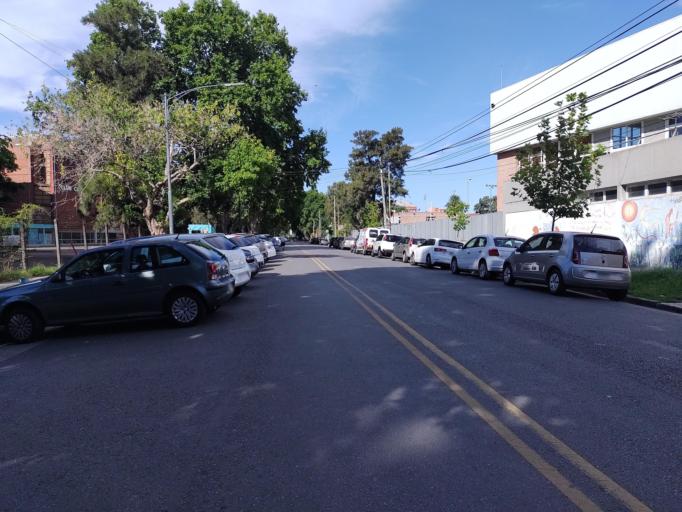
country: AR
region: Buenos Aires F.D.
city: Colegiales
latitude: -34.5442
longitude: -58.4587
